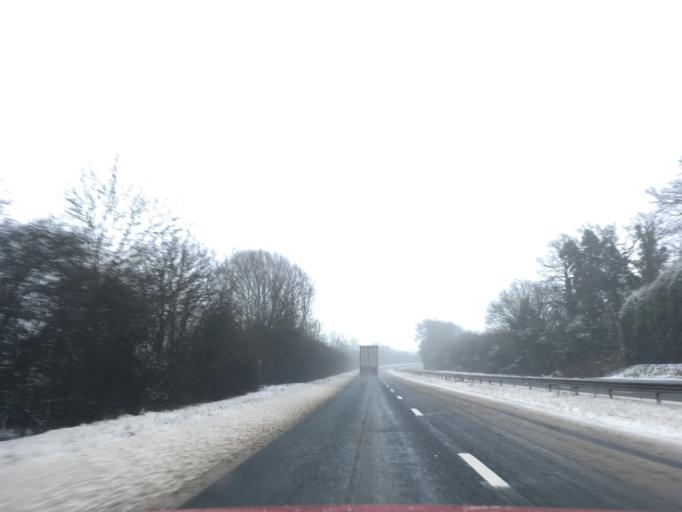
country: GB
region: England
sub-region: Warwickshire
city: Warwick
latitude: 52.2519
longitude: -1.6352
